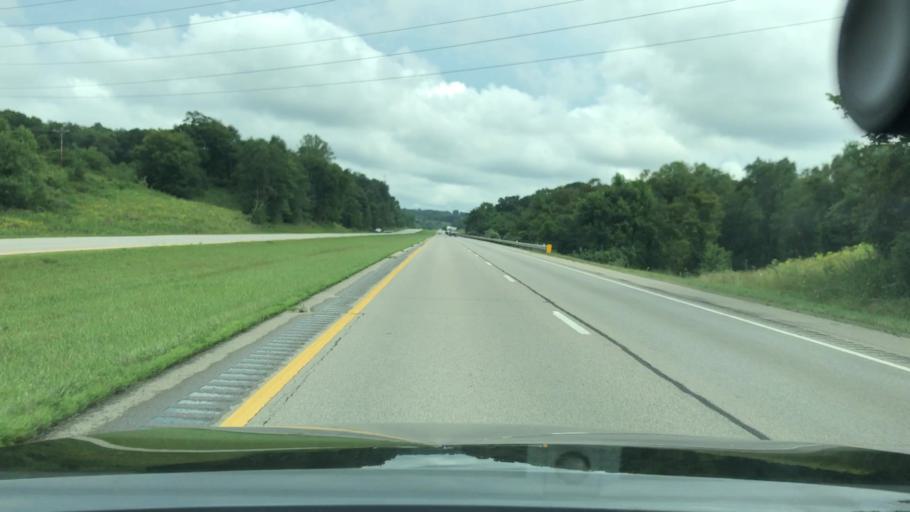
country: US
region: Ohio
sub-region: Jackson County
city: Oak Hill
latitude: 38.9466
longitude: -82.4771
